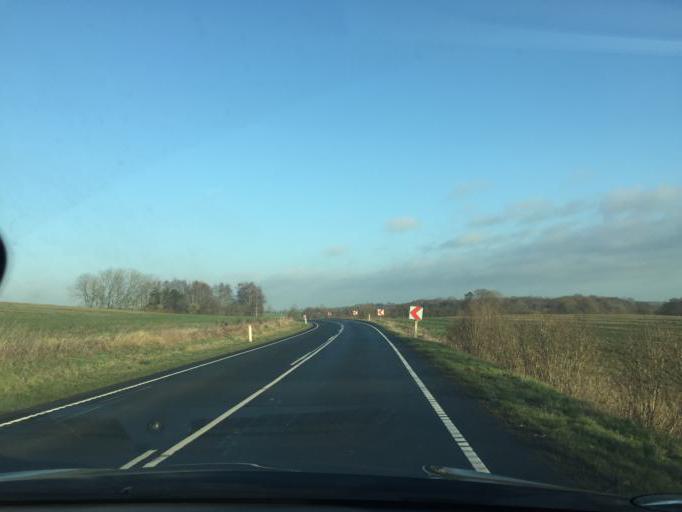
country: DK
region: South Denmark
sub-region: Faaborg-Midtfyn Kommune
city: Faaborg
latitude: 55.1721
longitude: 10.2877
